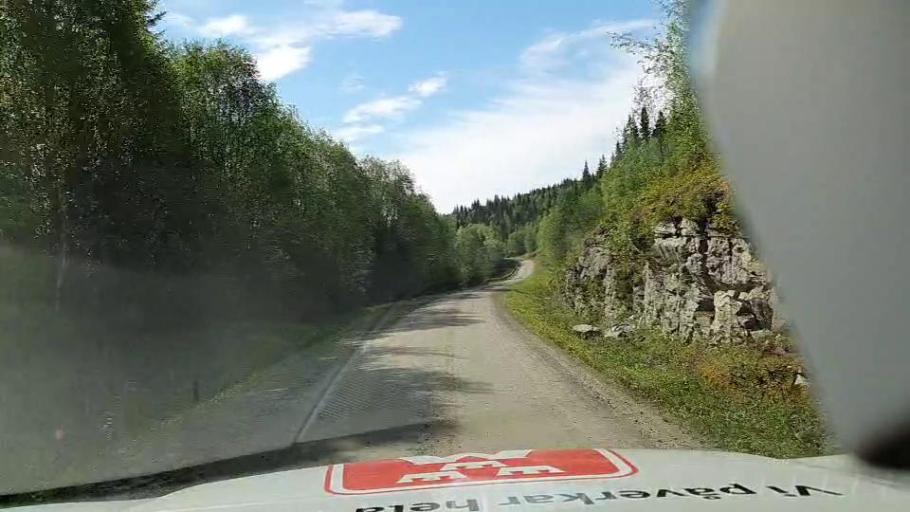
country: NO
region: Nord-Trondelag
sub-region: Lierne
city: Sandvika
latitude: 64.5723
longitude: 13.9022
